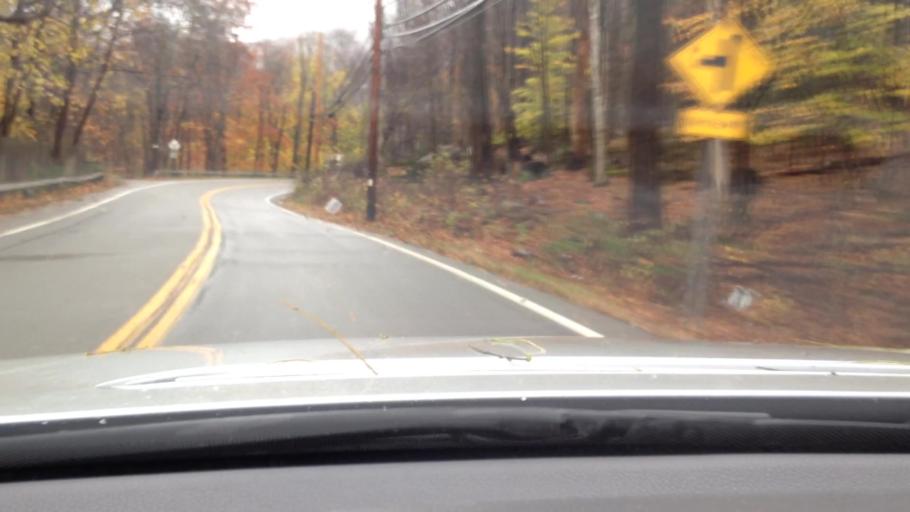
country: US
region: New York
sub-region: Orange County
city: West Point
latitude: 41.3738
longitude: -73.9380
